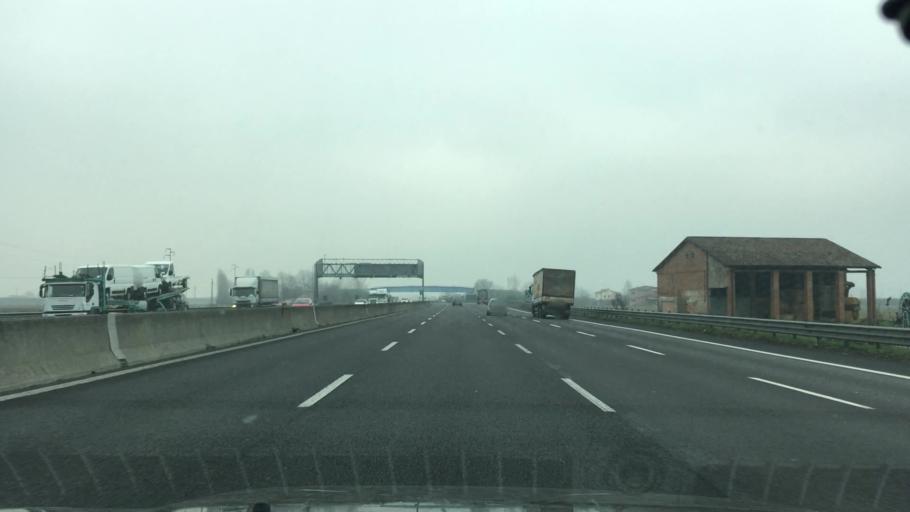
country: IT
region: Emilia-Romagna
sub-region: Provincia di Modena
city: San Vito
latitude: 44.5752
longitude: 10.9947
